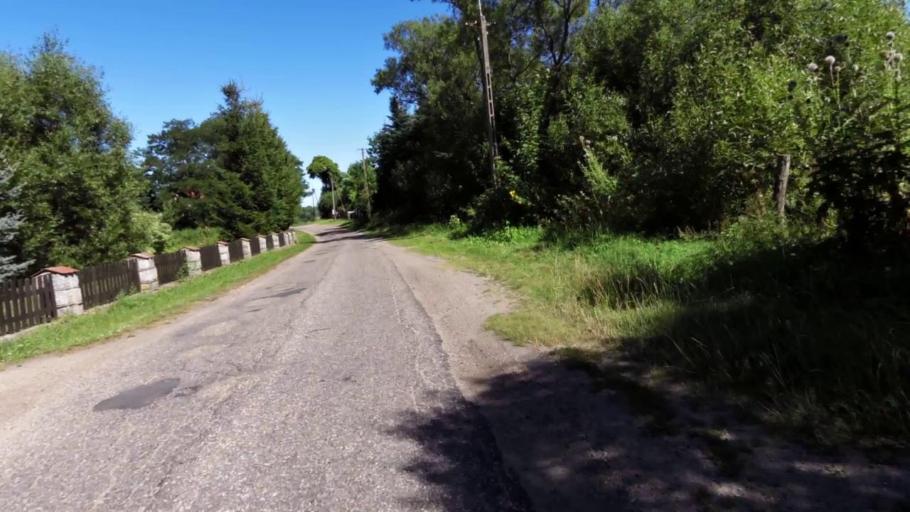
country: PL
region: West Pomeranian Voivodeship
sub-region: Powiat szczecinecki
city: Borne Sulinowo
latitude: 53.6720
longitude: 16.5655
